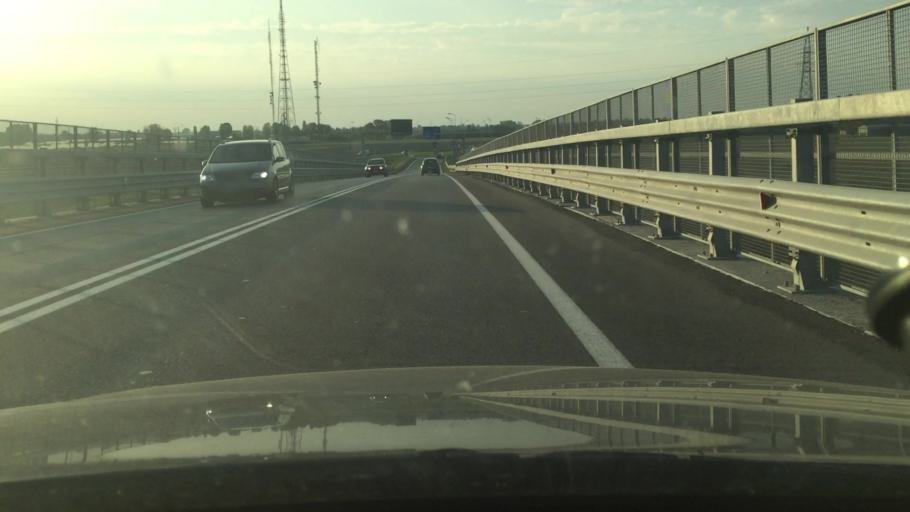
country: IT
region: Emilia-Romagna
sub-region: Provincia di Ferrara
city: Ferrara
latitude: 44.8257
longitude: 11.5857
